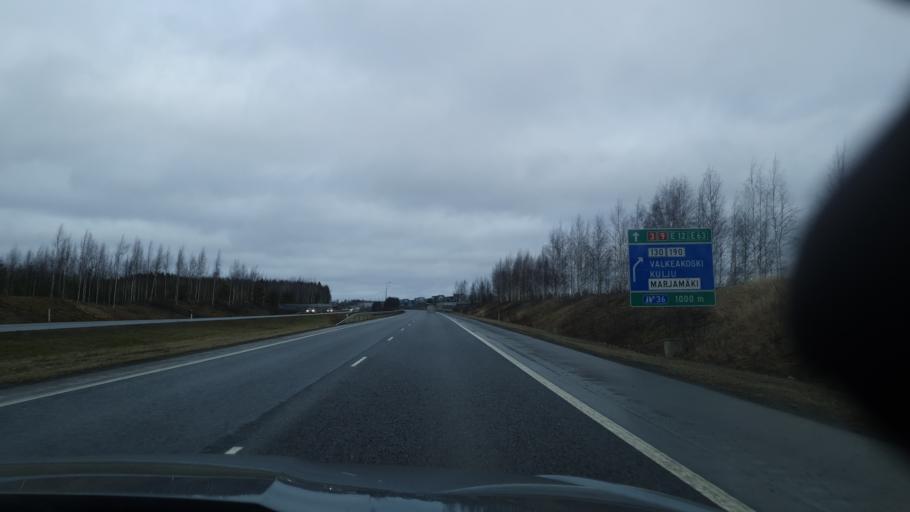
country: FI
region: Pirkanmaa
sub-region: Tampere
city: Lempaeaelae
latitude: 61.3539
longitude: 23.7910
